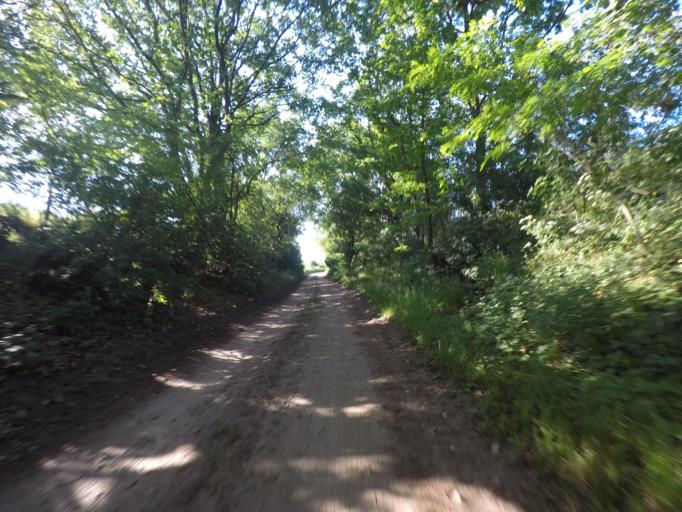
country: DE
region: Brandenburg
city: Marienwerder
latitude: 52.8623
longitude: 13.6832
